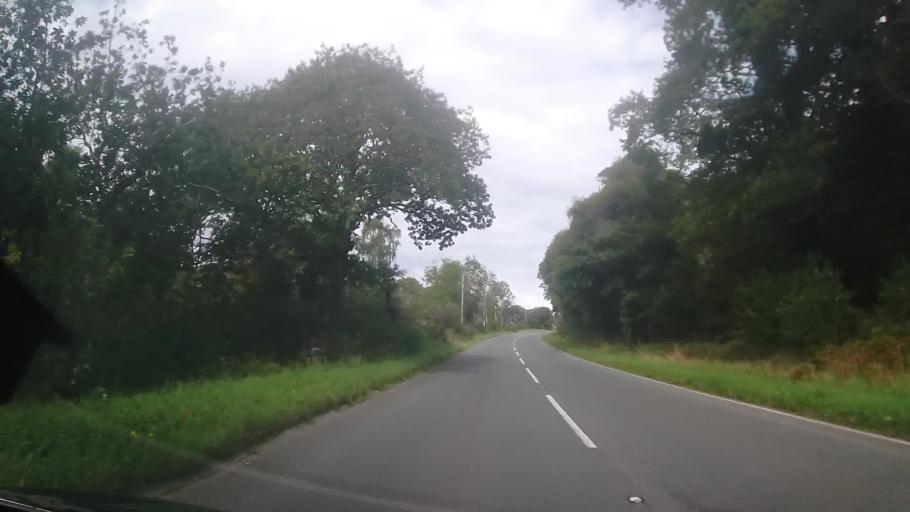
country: GB
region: Wales
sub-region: Gwynedd
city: Barmouth
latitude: 52.7323
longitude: -3.9751
